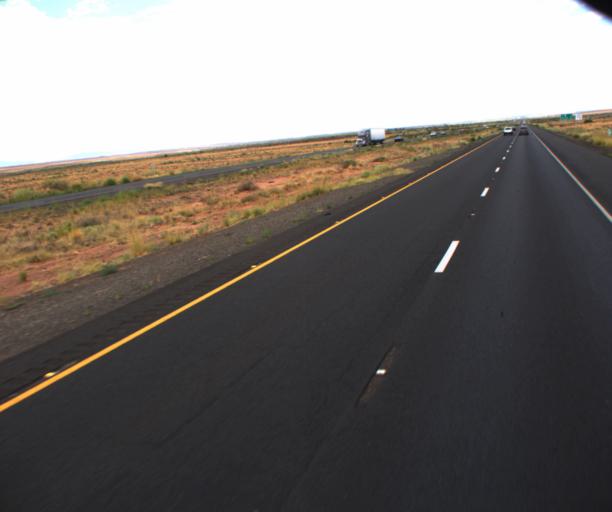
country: US
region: Arizona
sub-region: Navajo County
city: Winslow
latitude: 34.9794
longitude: -110.5375
